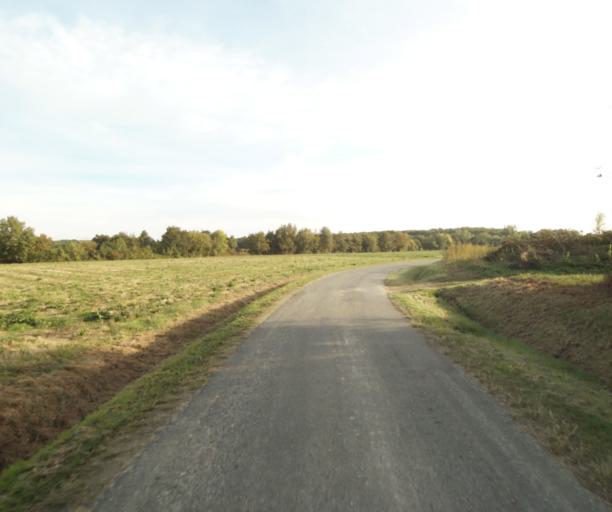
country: FR
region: Midi-Pyrenees
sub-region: Departement du Tarn-et-Garonne
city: Campsas
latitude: 43.8742
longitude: 1.3505
